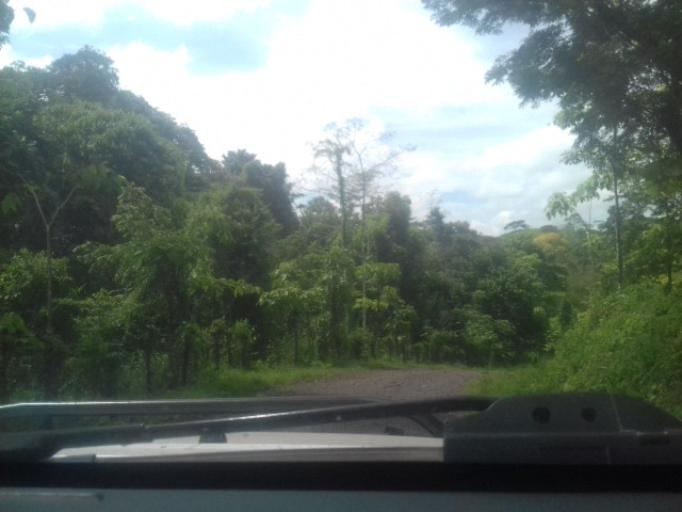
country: NI
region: Atlantico Norte (RAAN)
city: Waslala
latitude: 13.4987
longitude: -85.2317
